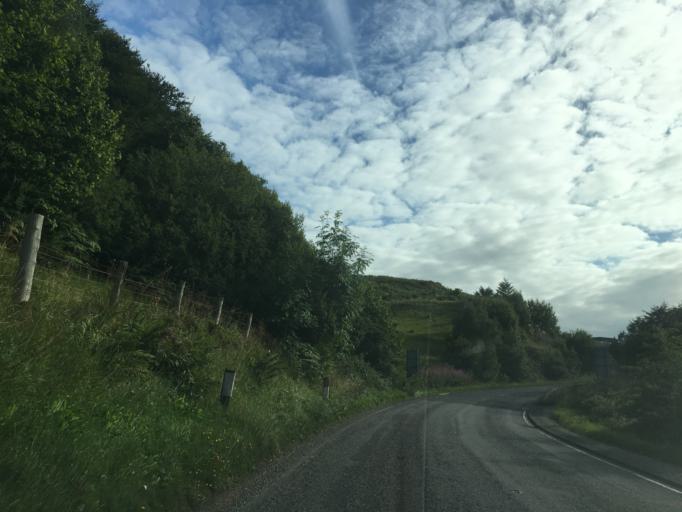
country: GB
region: Scotland
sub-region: Argyll and Bute
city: Oban
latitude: 56.3971
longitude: -5.4681
